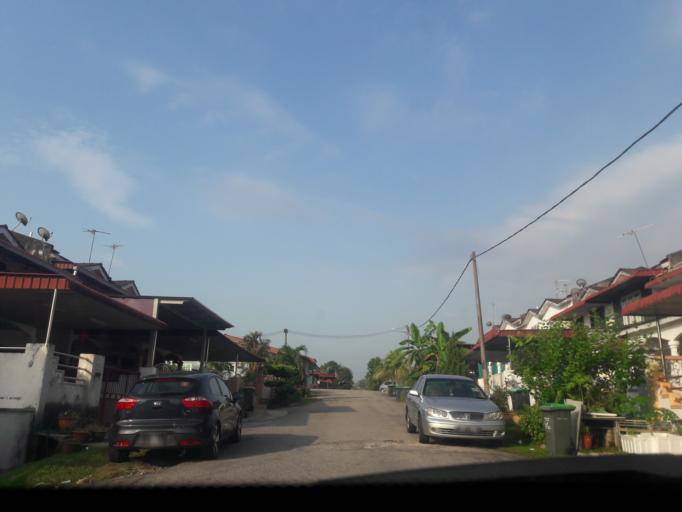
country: MY
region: Kedah
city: Kulim
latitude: 5.3770
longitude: 100.5356
